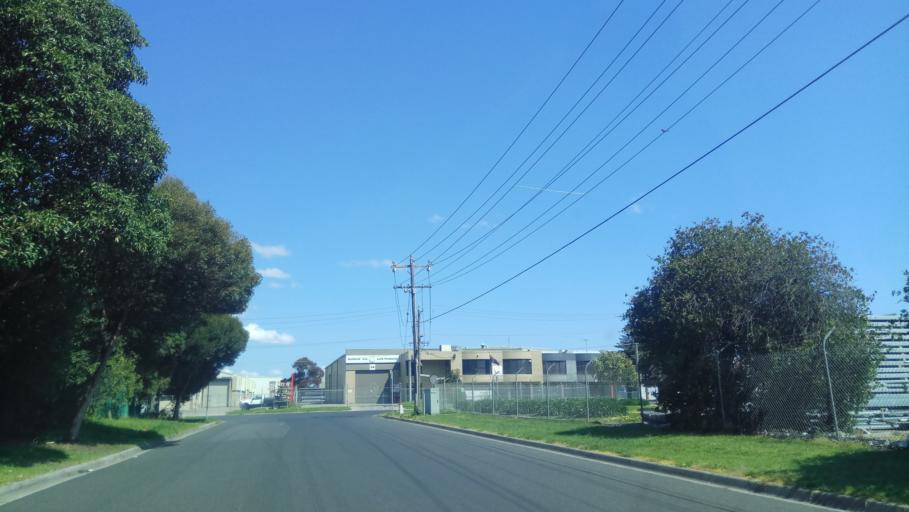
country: AU
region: Victoria
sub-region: Kingston
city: Dingley Village
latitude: -37.9890
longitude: 145.1154
